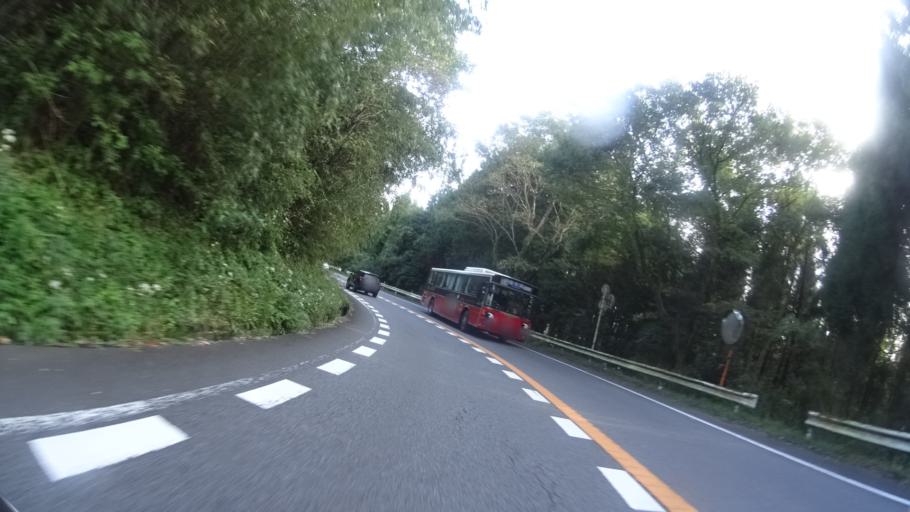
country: JP
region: Oita
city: Beppu
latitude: 33.2704
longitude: 131.4289
